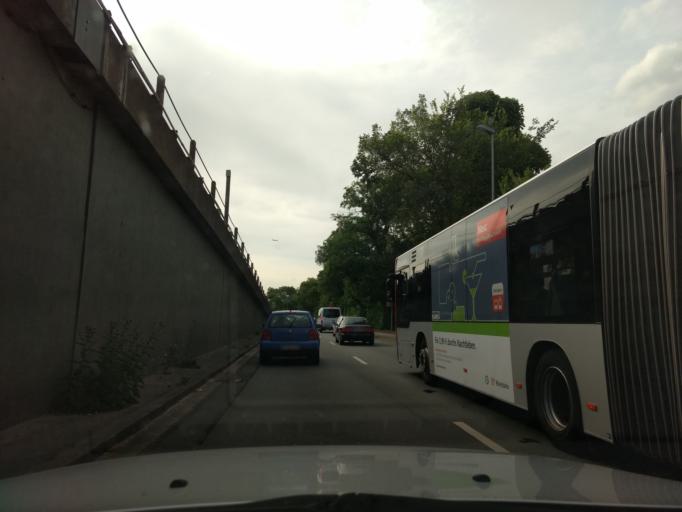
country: DE
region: North Rhine-Westphalia
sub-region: Regierungsbezirk Dusseldorf
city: Dusseldorf
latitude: 51.2542
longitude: 6.7700
